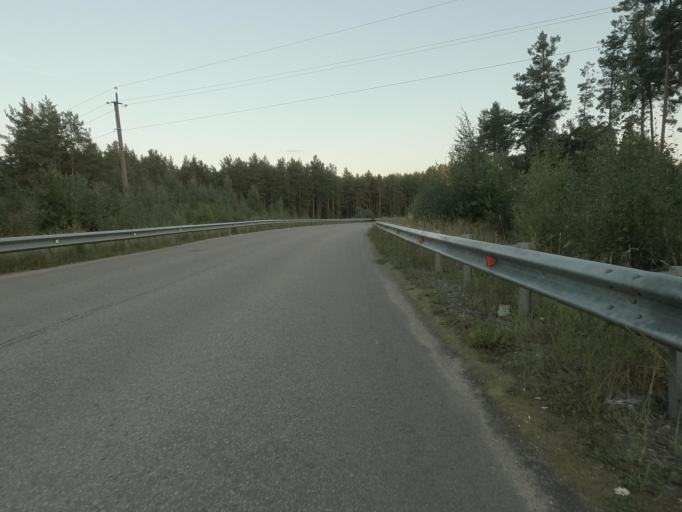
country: RU
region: Leningrad
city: Mga
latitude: 59.7623
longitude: 31.0397
